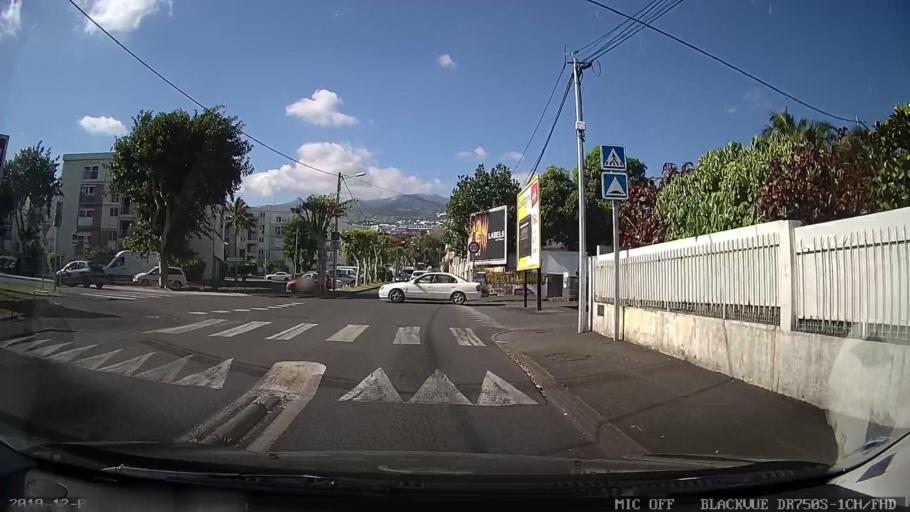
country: RE
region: Reunion
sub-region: Reunion
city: Saint-Denis
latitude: -20.8967
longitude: 55.4809
